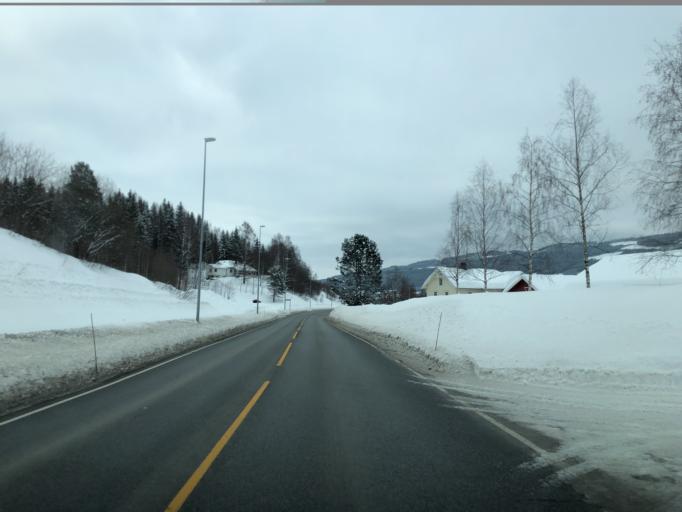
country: NO
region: Oppland
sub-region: Gausdal
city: Segalstad bru
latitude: 61.1793
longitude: 10.3251
